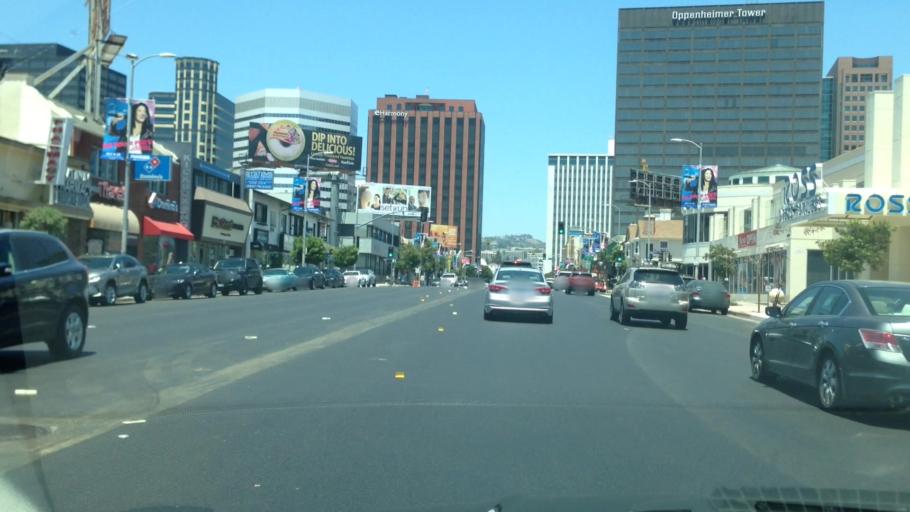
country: US
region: California
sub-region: Los Angeles County
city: Westwood, Los Angeles
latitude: 34.0554
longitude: -118.4418
